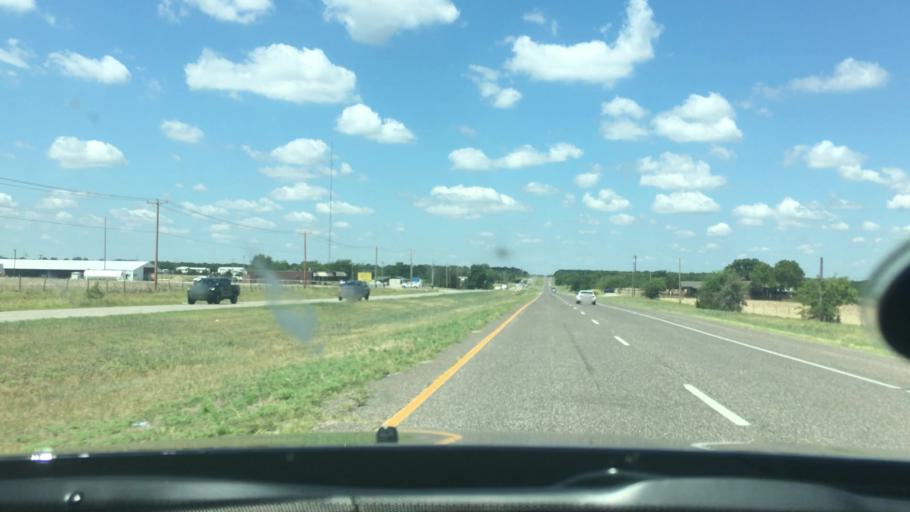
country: US
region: Oklahoma
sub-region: Carter County
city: Lone Grove
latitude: 34.1731
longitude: -97.2756
